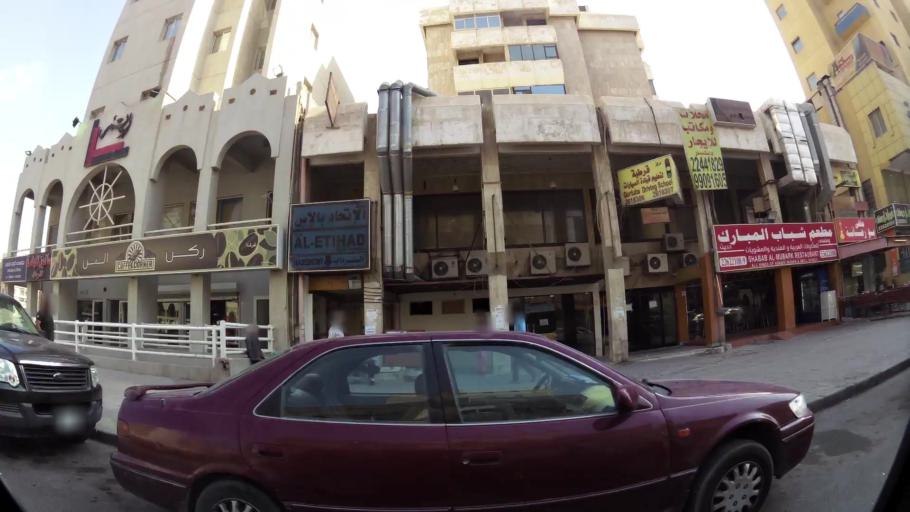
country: KW
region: Muhafazat Hawalli
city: Hawalli
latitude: 29.3312
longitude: 48.0186
